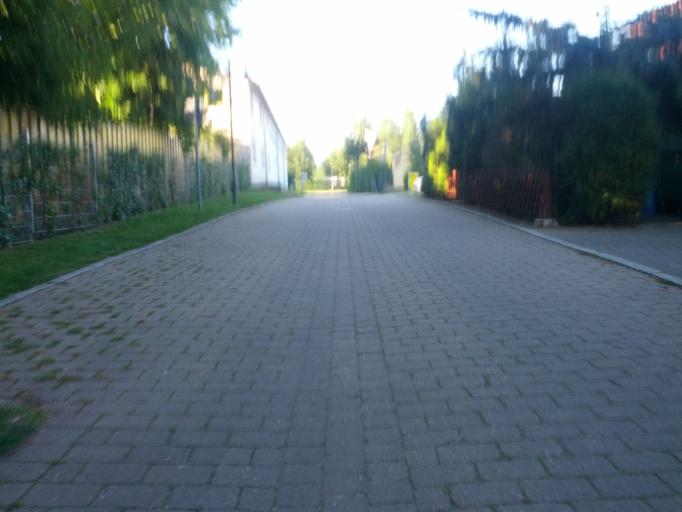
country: DE
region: Mecklenburg-Vorpommern
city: Bastorf
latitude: 54.1101
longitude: 11.6324
